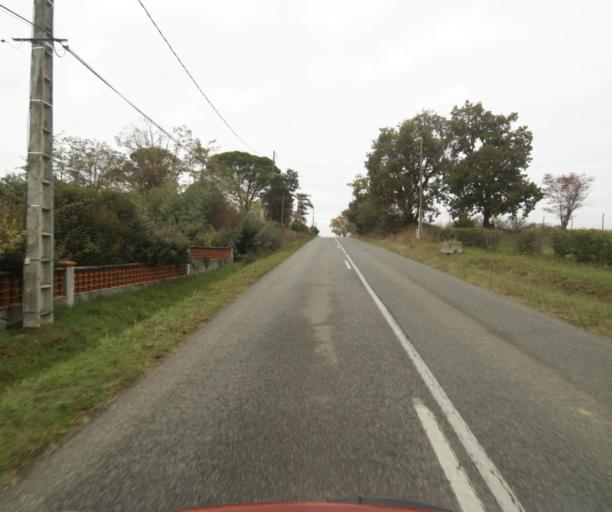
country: FR
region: Midi-Pyrenees
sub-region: Departement du Tarn-et-Garonne
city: Verdun-sur-Garonne
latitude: 43.8081
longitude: 1.2058
